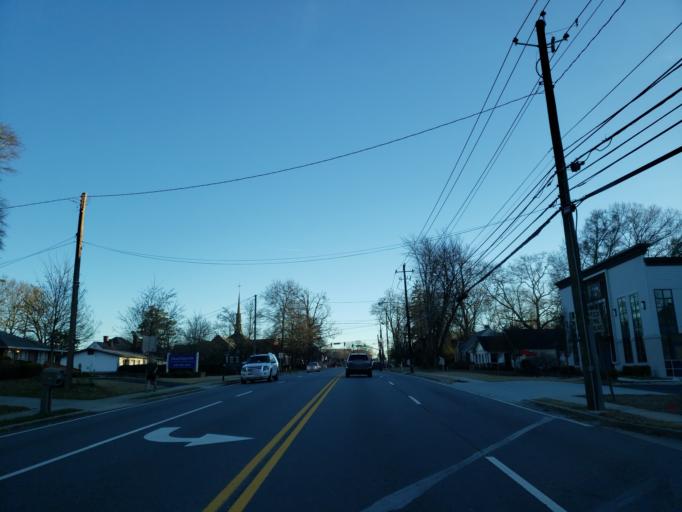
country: US
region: Georgia
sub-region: Fulton County
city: Alpharetta
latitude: 34.0800
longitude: -84.2946
